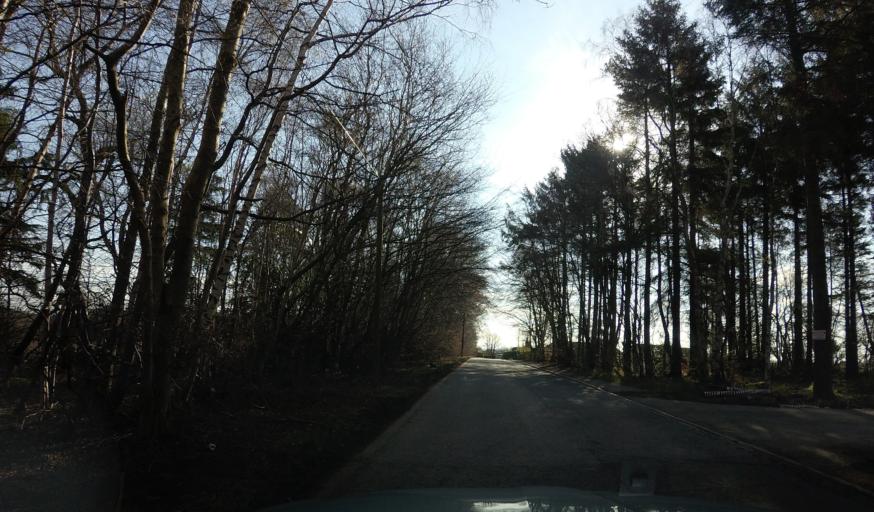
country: GB
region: Scotland
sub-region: Midlothian
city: Penicuik
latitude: 55.8475
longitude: -3.2193
